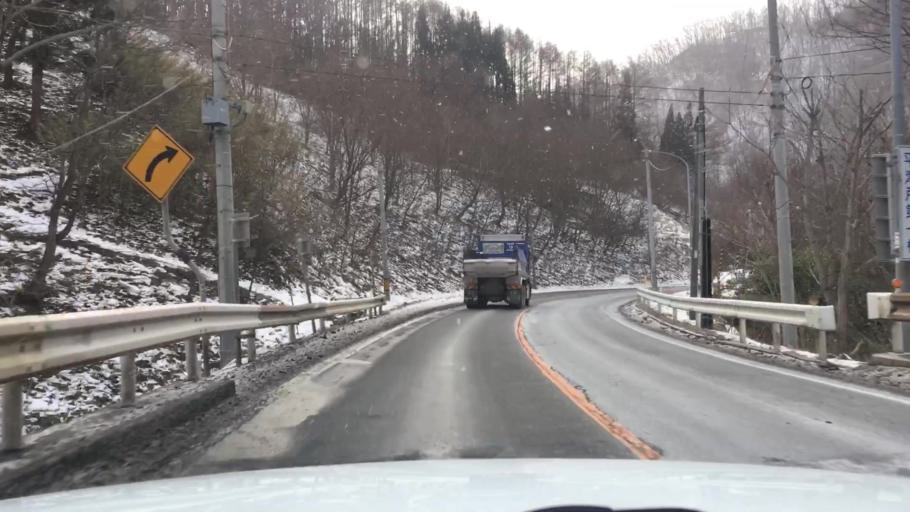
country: JP
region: Iwate
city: Tono
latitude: 39.6222
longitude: 141.5082
